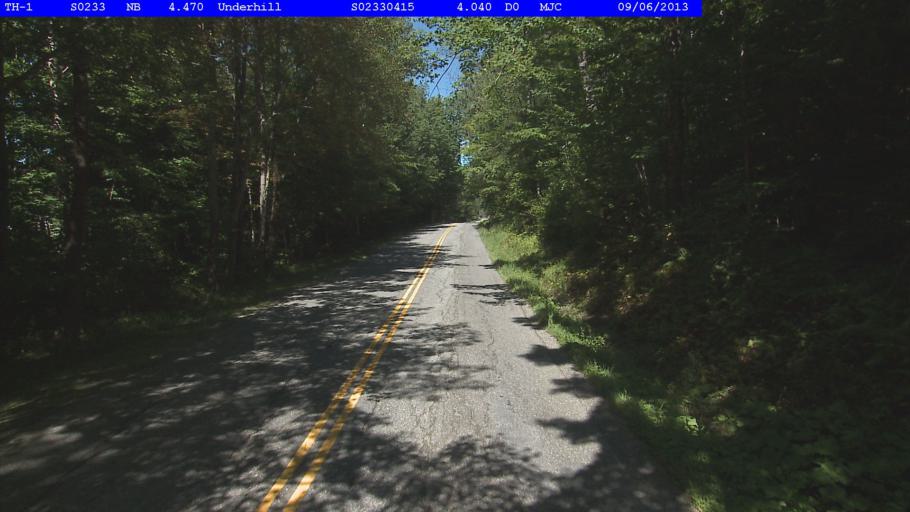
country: US
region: Vermont
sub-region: Chittenden County
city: Jericho
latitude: 44.5251
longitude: -72.8796
